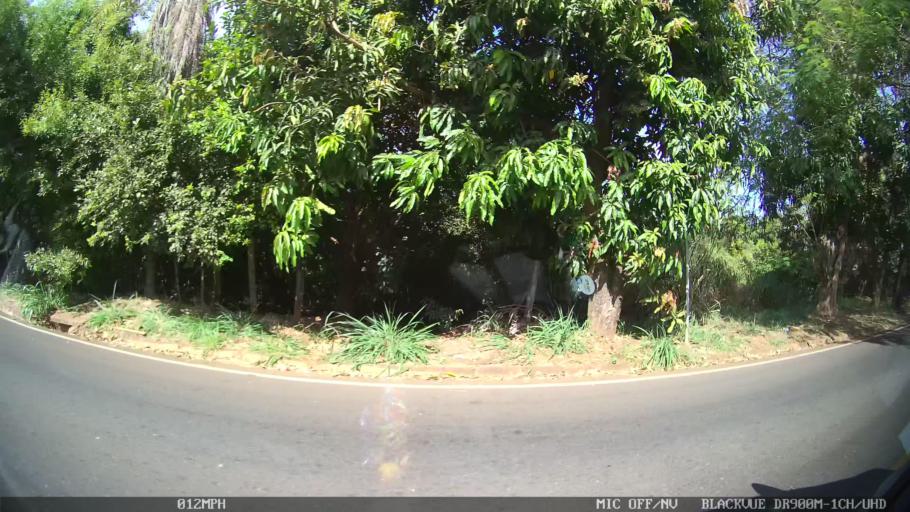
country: BR
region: Sao Paulo
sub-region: Sao Jose Do Rio Preto
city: Sao Jose do Rio Preto
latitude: -20.8477
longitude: -49.3617
